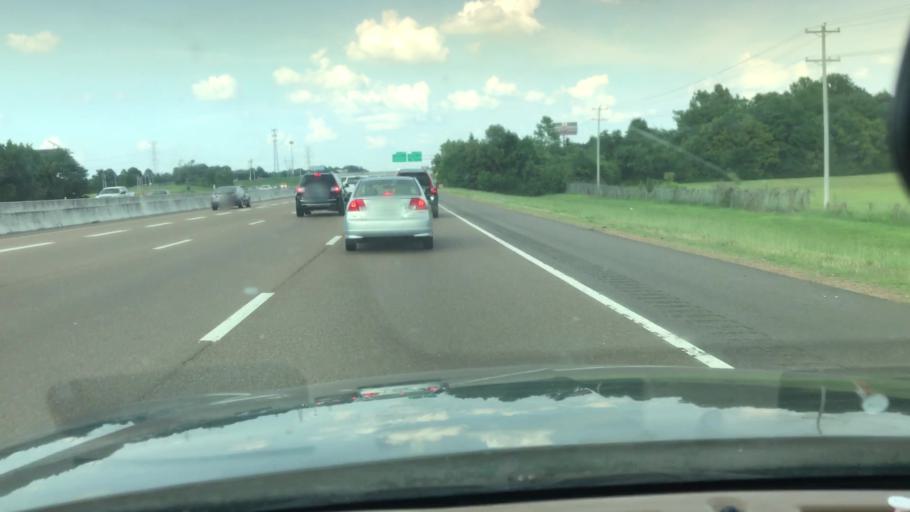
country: US
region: Tennessee
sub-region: Shelby County
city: Bartlett
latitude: 35.1828
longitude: -89.8192
